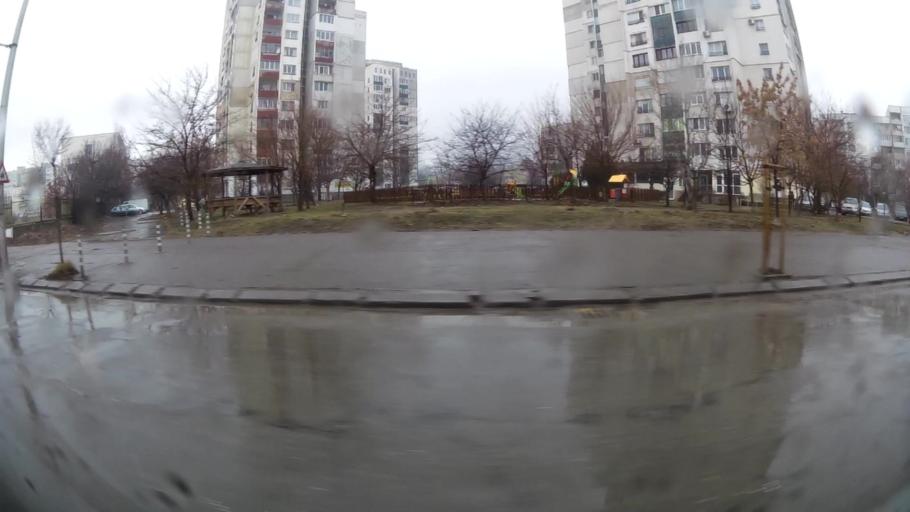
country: BG
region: Sofia-Capital
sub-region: Stolichna Obshtina
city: Sofia
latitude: 42.6540
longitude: 23.4019
